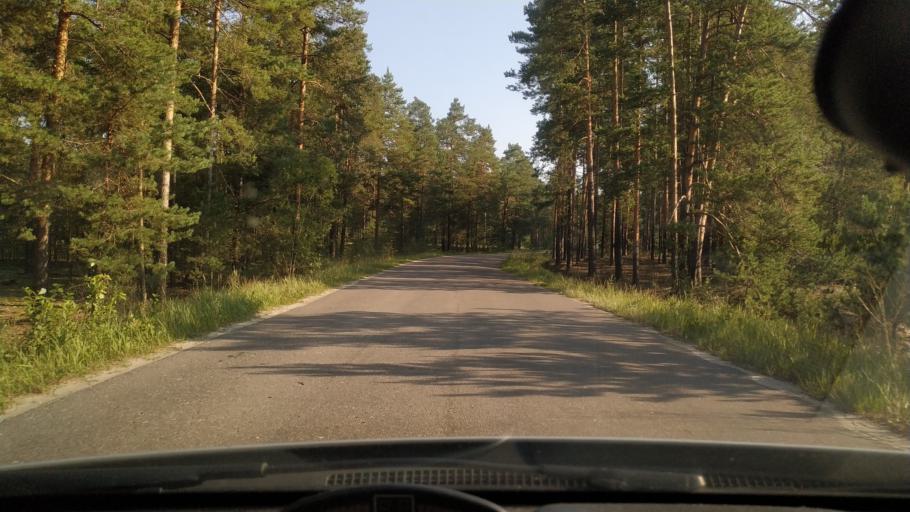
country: RU
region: Moskovskaya
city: Roshal'
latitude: 55.6559
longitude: 39.8009
